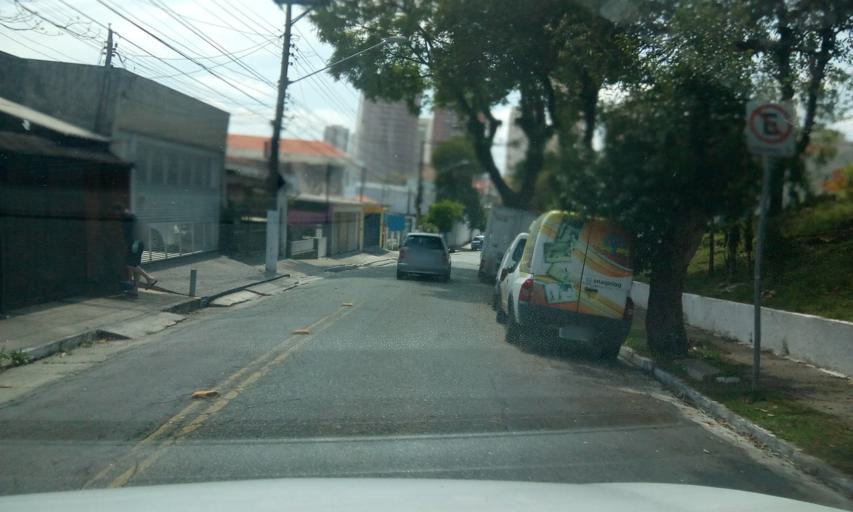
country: BR
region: Sao Paulo
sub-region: Sao Paulo
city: Sao Paulo
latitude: -23.5315
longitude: -46.7019
